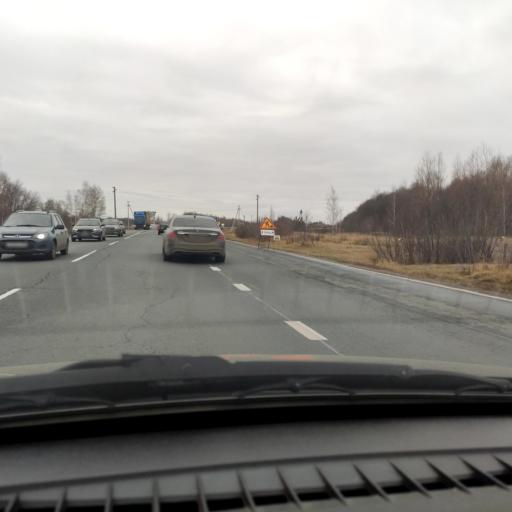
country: RU
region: Samara
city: Zhigulevsk
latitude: 53.3431
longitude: 49.4480
